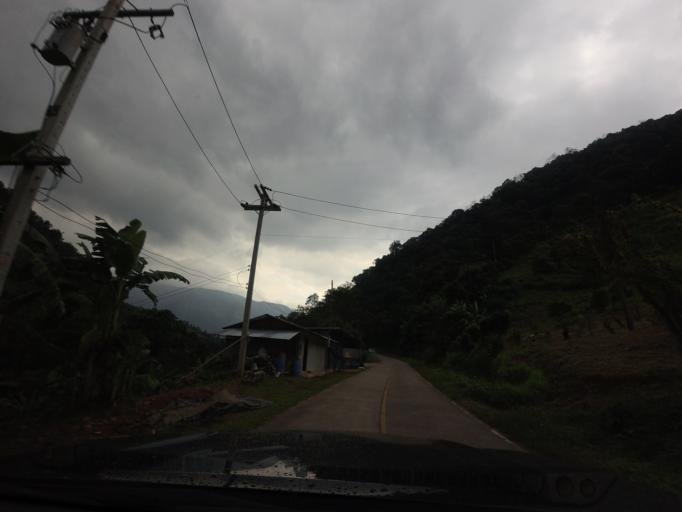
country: TH
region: Nan
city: Bo Kluea
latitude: 19.1964
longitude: 101.1900
